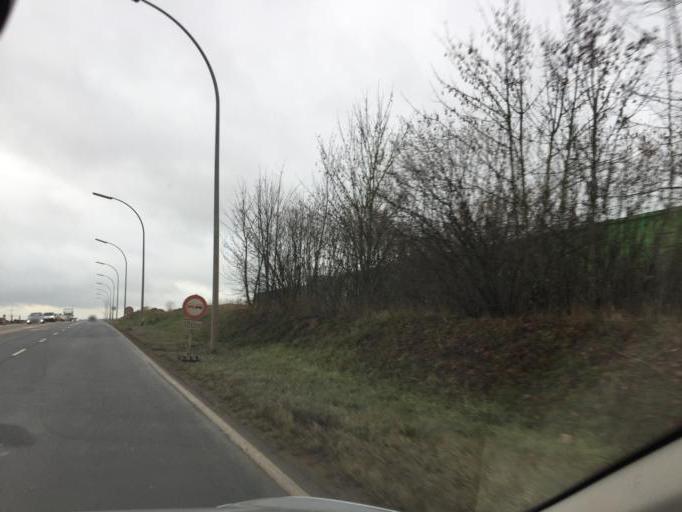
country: LU
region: Diekirch
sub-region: Canton de Diekirch
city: Diekirch
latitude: 49.8823
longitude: 6.1349
